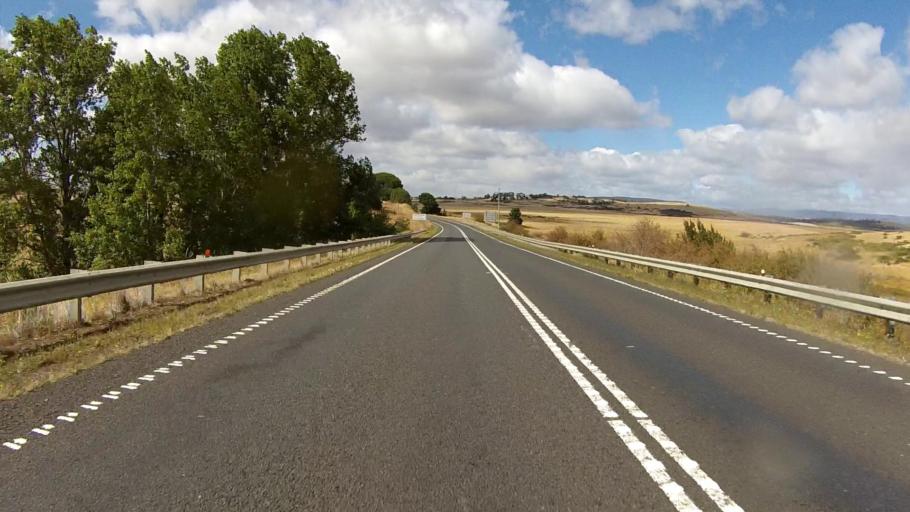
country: AU
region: Tasmania
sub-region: Northern Midlands
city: Evandale
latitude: -41.8416
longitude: 147.4481
